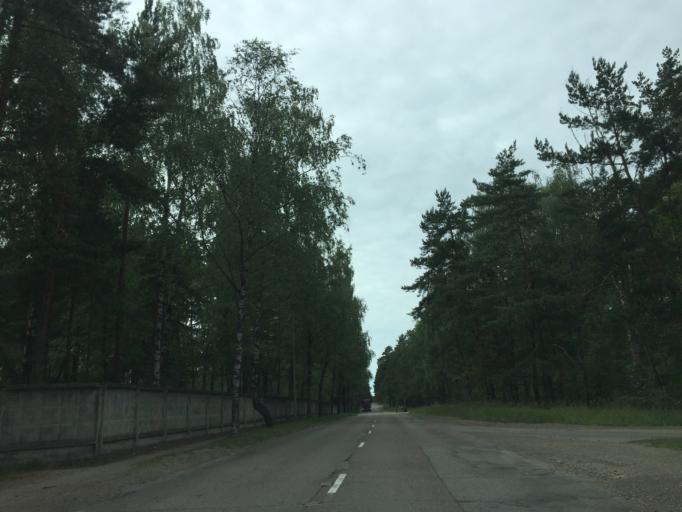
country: LV
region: Riga
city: Jaunciems
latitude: 57.0186
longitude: 24.2081
